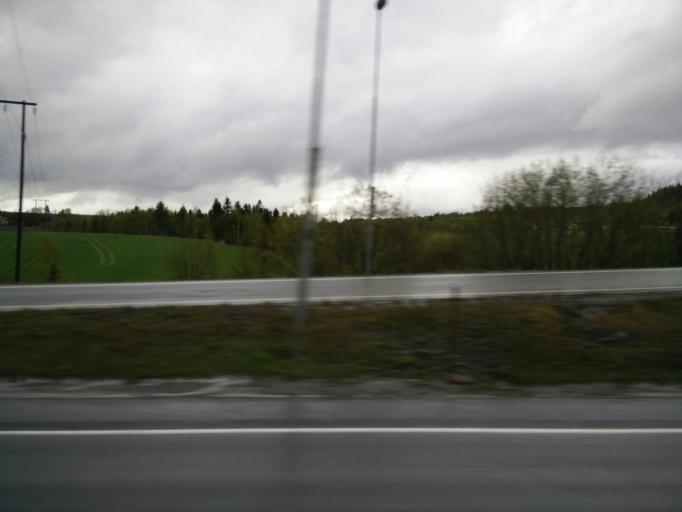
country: NO
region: Sor-Trondelag
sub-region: Malvik
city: Malvik
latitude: 63.4225
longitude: 10.6276
